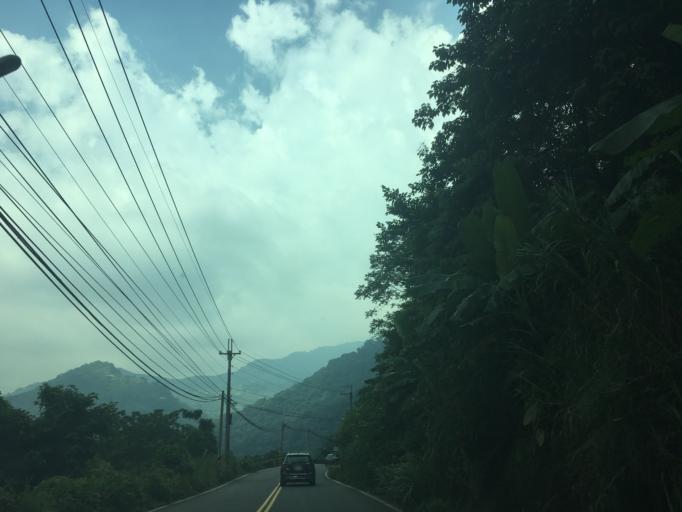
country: TW
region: Taiwan
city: Fengyuan
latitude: 24.2953
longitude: 120.9159
